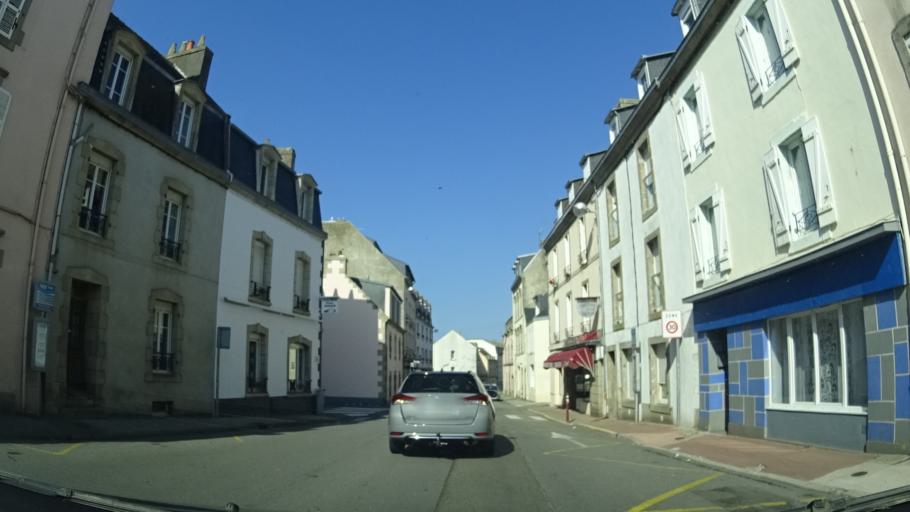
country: FR
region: Brittany
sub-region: Departement du Finistere
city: Douarnenez
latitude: 48.0898
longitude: -4.3254
